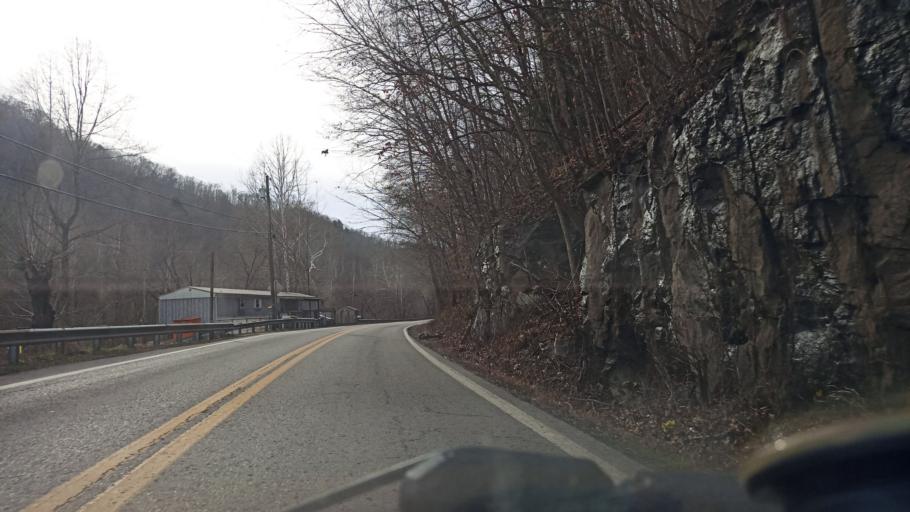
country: US
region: West Virginia
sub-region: Logan County
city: Mallory
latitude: 37.6518
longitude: -81.8519
